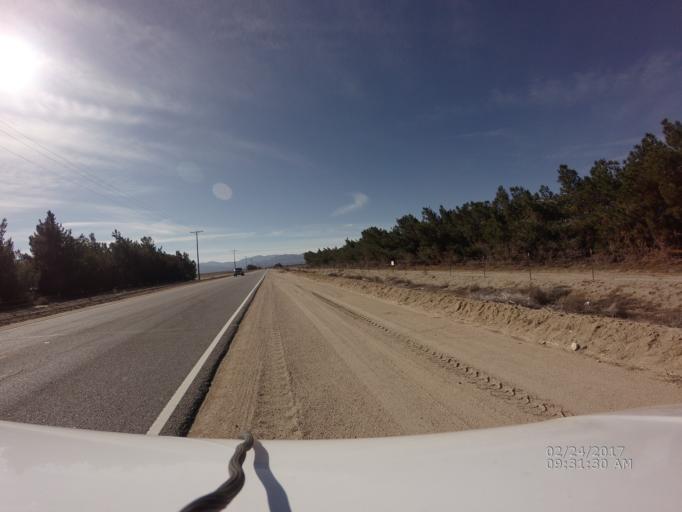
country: US
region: California
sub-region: Los Angeles County
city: Palmdale
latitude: 34.6187
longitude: -118.0410
